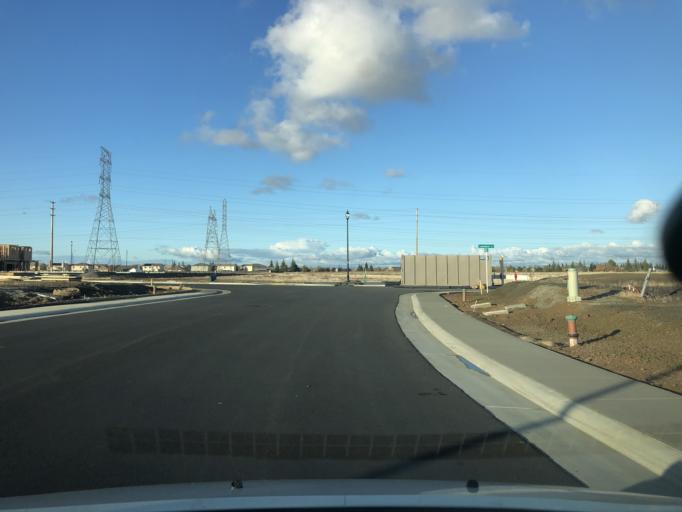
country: US
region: California
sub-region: Sacramento County
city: Antelope
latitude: 38.7622
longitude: -121.3624
